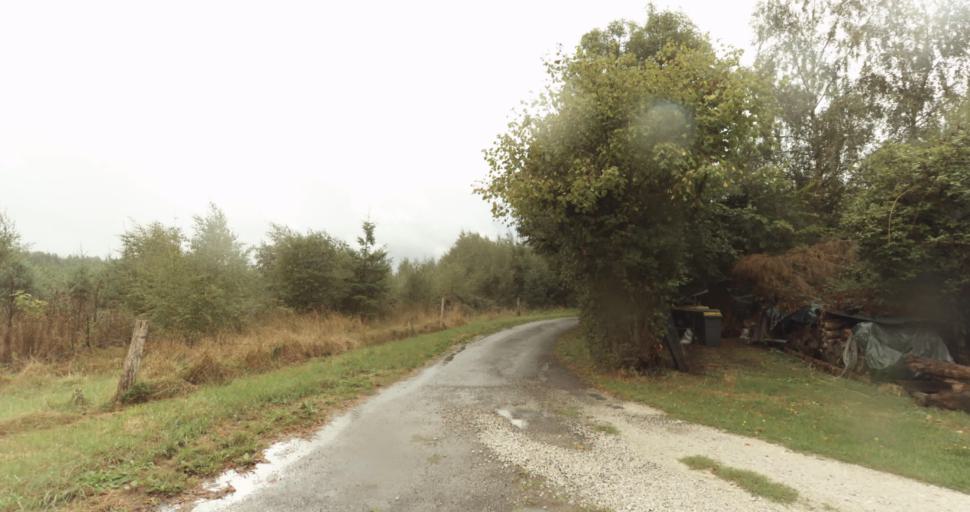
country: FR
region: Lower Normandy
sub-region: Departement de l'Orne
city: Sainte-Gauburge-Sainte-Colombe
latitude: 48.6953
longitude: 0.4211
